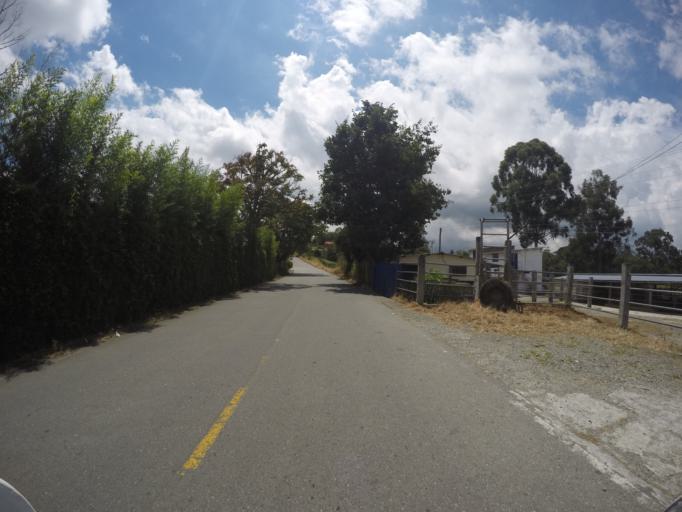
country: CO
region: Quindio
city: Filandia
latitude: 4.6410
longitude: -75.6847
